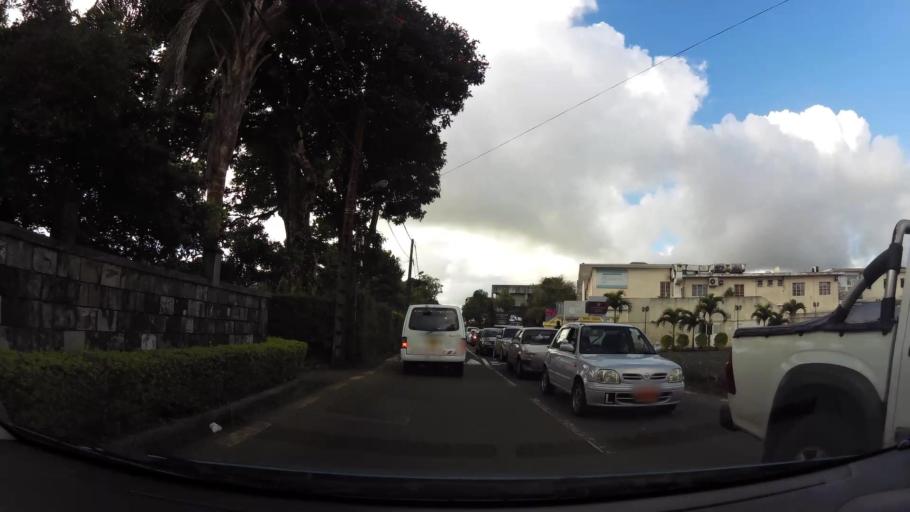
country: MU
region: Plaines Wilhems
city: Curepipe
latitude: -20.3209
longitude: 57.5197
